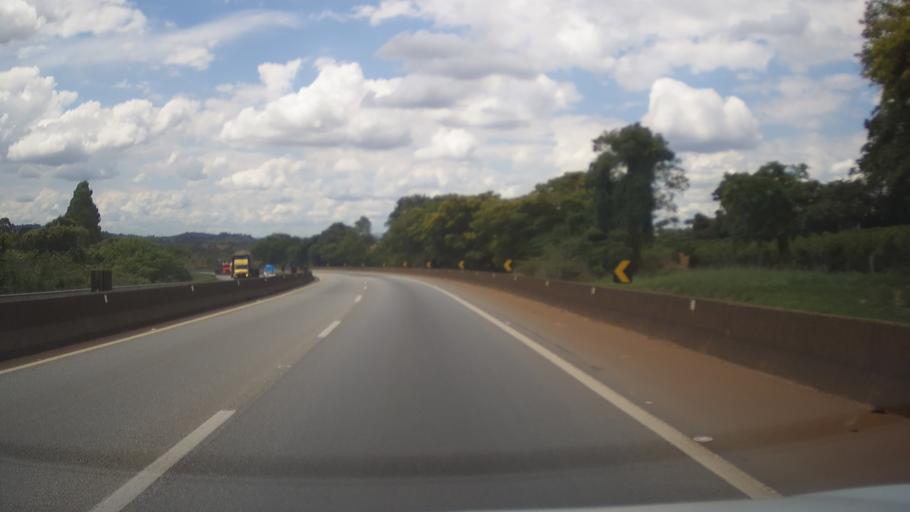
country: BR
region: Minas Gerais
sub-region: Nepomuceno
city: Nepomuceno
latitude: -21.2434
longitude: -45.1360
